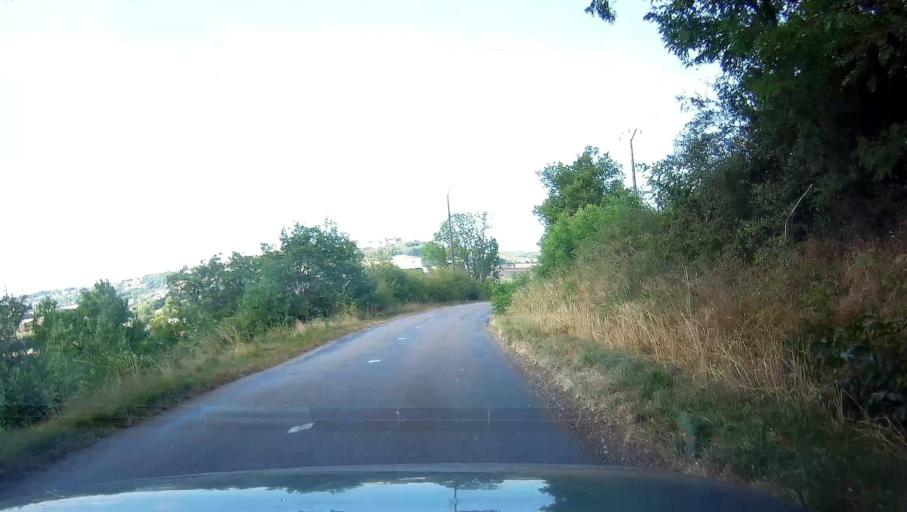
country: FR
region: Champagne-Ardenne
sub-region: Departement de la Haute-Marne
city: Langres
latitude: 47.8738
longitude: 5.3605
